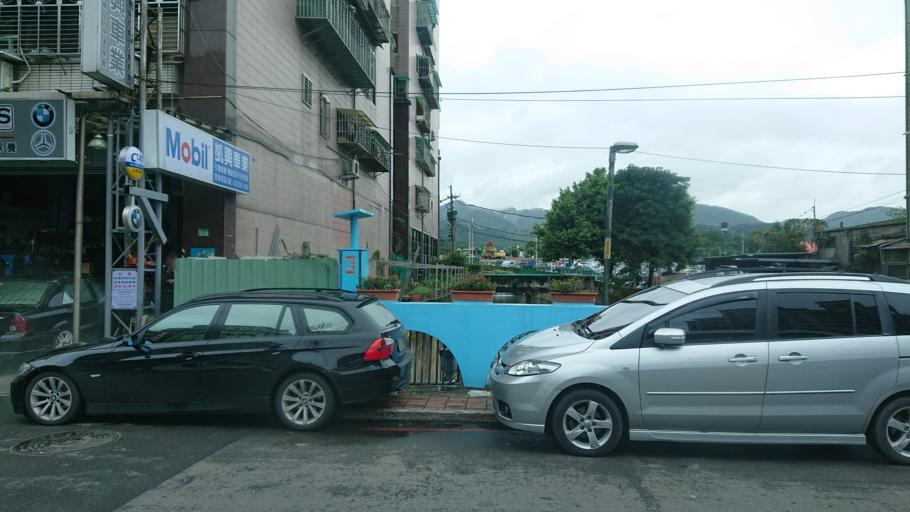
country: TW
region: Taipei
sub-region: Taipei
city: Banqiao
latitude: 24.9816
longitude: 121.4561
